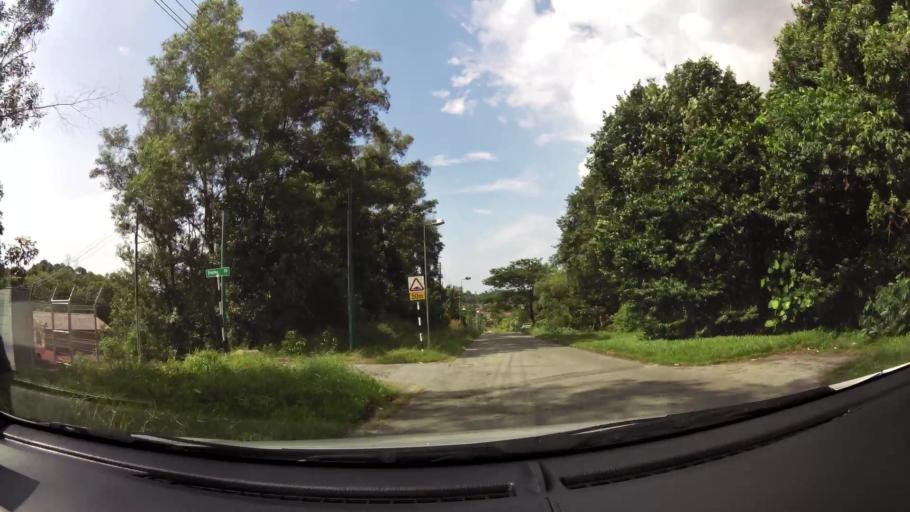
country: BN
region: Brunei and Muara
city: Bandar Seri Begawan
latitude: 4.9568
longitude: 114.9511
